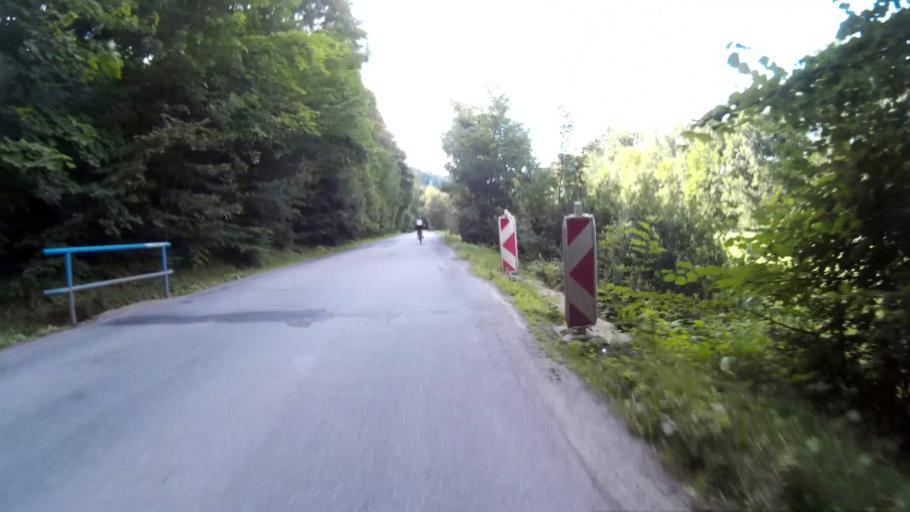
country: CZ
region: South Moravian
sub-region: Okres Brno-Venkov
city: Rosice
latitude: 49.1638
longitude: 16.4239
